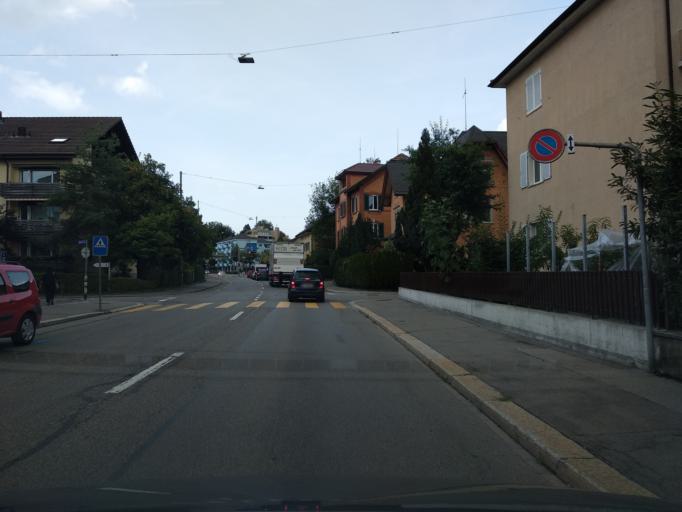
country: CH
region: Zurich
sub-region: Bezirk Winterthur
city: Veltheim (Kreis 5) / Blumenau
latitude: 47.5079
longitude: 8.7232
